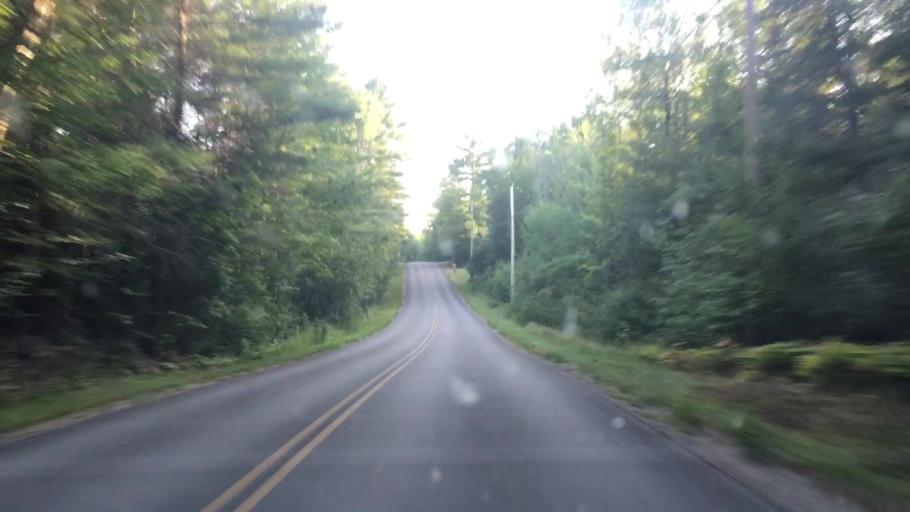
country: US
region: Maine
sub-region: Penobscot County
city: Hampden
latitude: 44.7013
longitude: -68.8931
